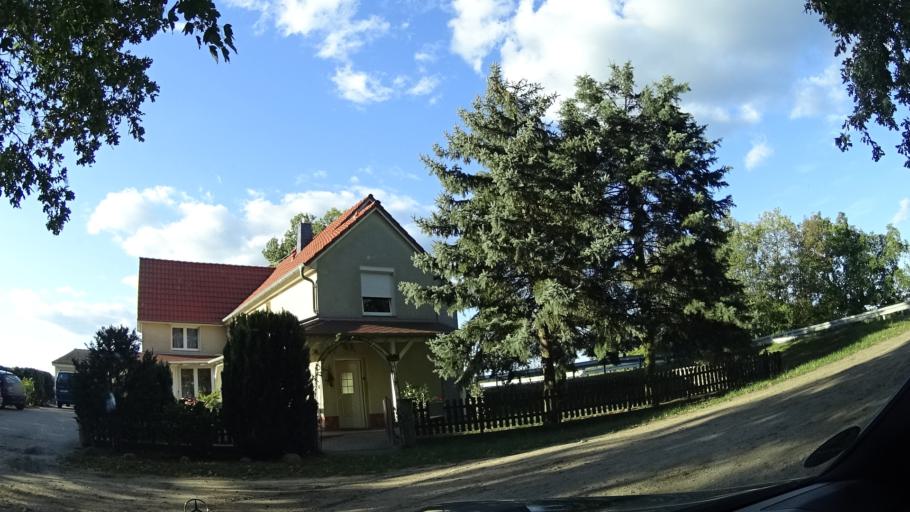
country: DE
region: Brandenburg
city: Neuruppin
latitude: 52.9684
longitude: 12.7564
